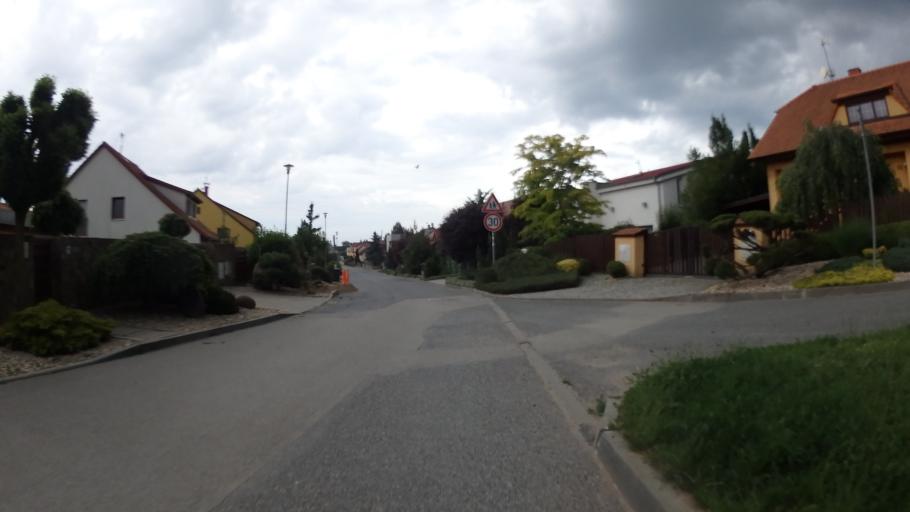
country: CZ
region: South Moravian
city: Ostopovice
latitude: 49.1391
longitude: 16.5523
